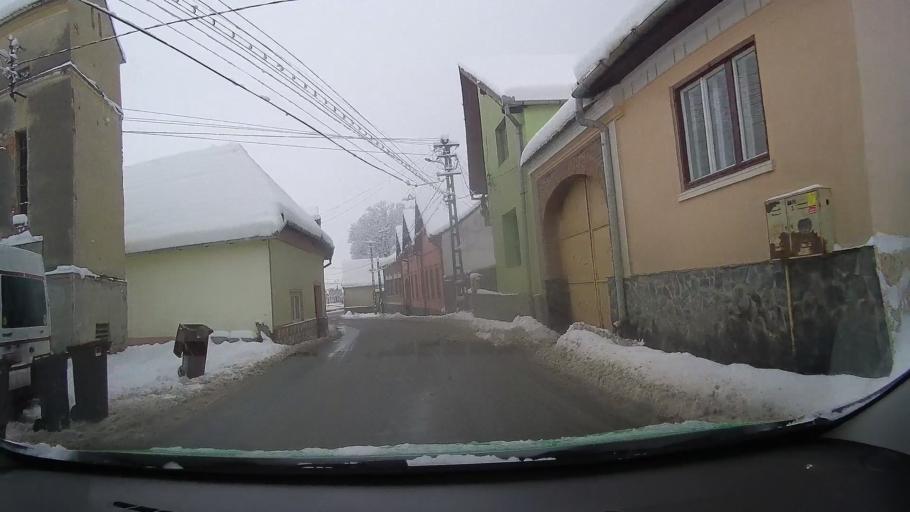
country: RO
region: Sibiu
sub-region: Oras Saliste
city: Saliste
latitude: 45.7948
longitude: 23.8739
